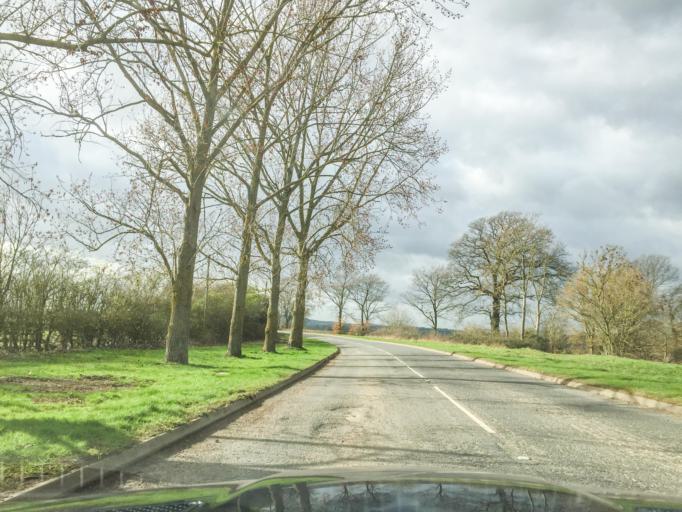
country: GB
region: England
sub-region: Warwickshire
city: Shipston on Stour
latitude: 52.0622
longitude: -1.5765
